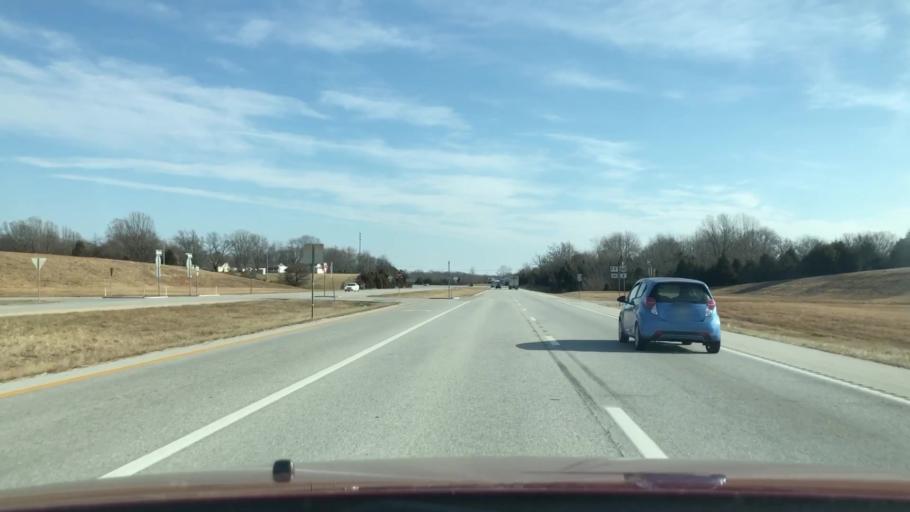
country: US
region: Missouri
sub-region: Webster County
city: Rogersville
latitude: 37.1517
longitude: -92.9442
